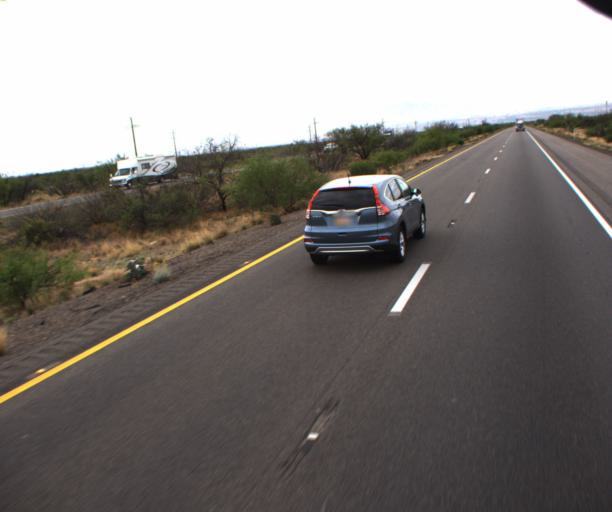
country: US
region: Arizona
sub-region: Cochise County
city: Saint David
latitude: 31.9996
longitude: -110.1579
